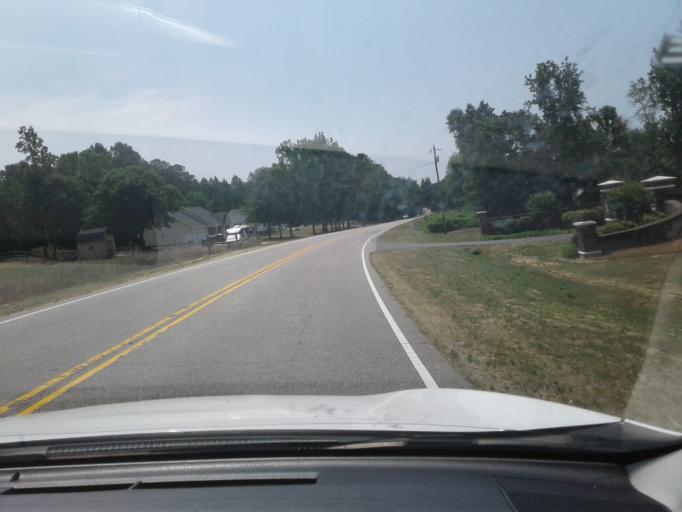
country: US
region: North Carolina
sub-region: Harnett County
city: Coats
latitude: 35.4371
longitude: -78.6807
